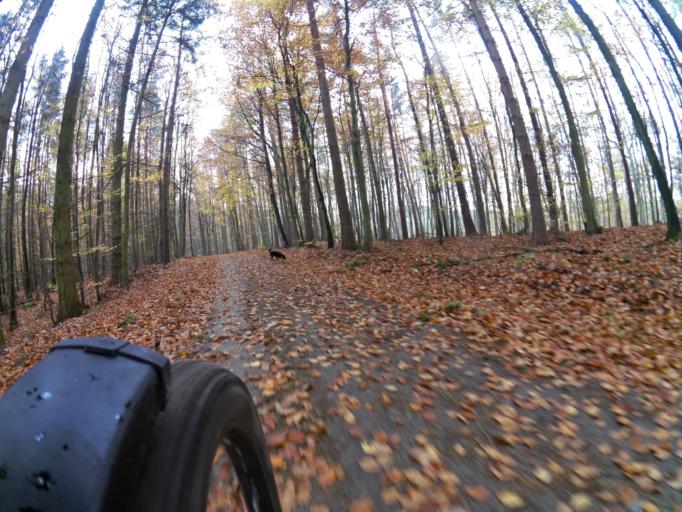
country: PL
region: Pomeranian Voivodeship
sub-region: Powiat pucki
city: Krokowa
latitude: 54.7729
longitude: 18.0923
